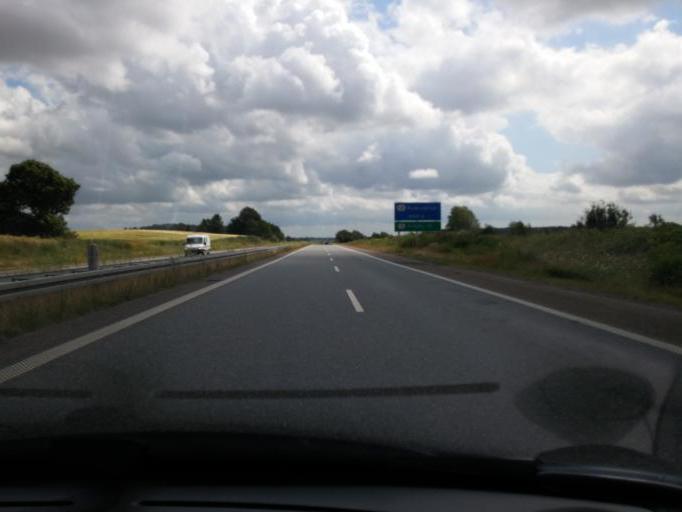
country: DK
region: South Denmark
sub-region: Faaborg-Midtfyn Kommune
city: Ringe
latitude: 55.2061
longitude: 10.5109
